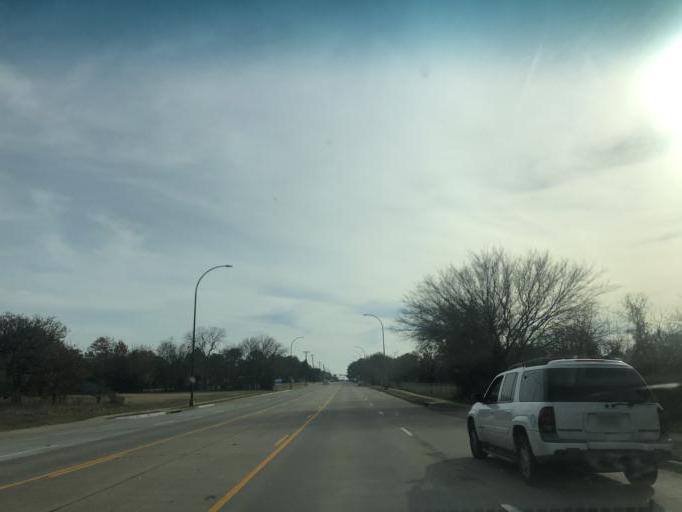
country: US
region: Texas
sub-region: Tarrant County
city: Dalworthington Gardens
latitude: 32.6900
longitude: -97.1494
